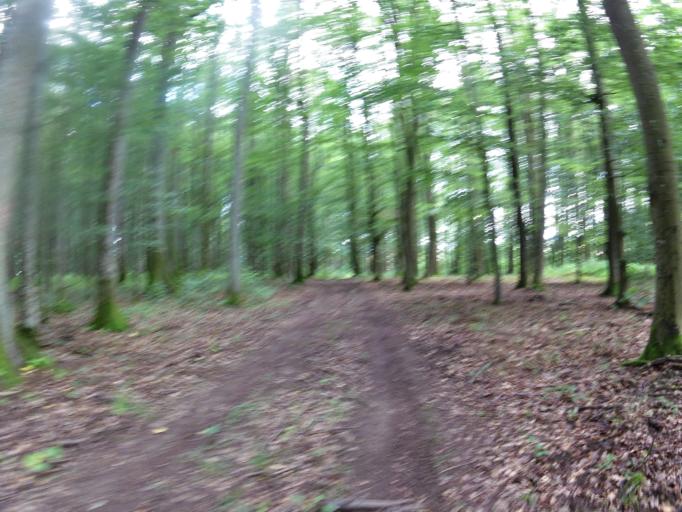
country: DE
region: Bavaria
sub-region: Regierungsbezirk Unterfranken
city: Kleinrinderfeld
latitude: 49.7028
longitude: 9.8748
